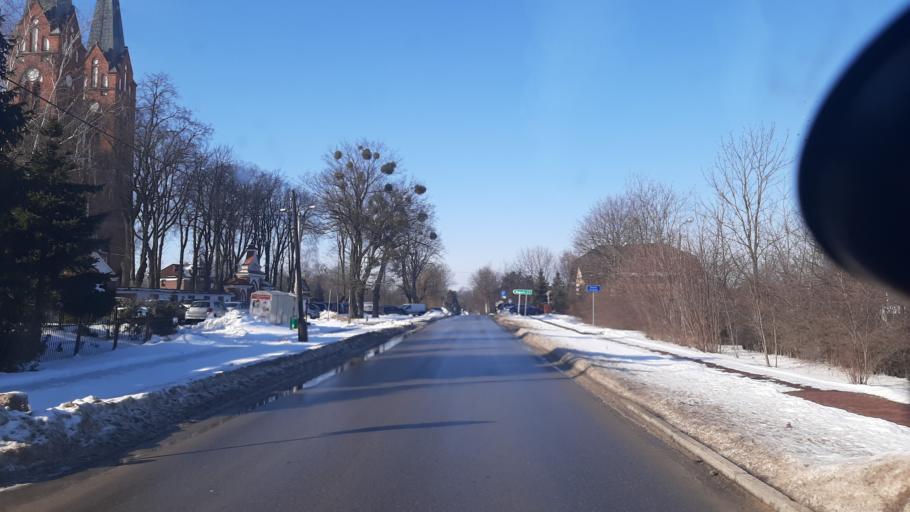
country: PL
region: Lublin Voivodeship
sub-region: Powiat lubelski
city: Garbow
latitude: 51.3511
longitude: 22.3468
